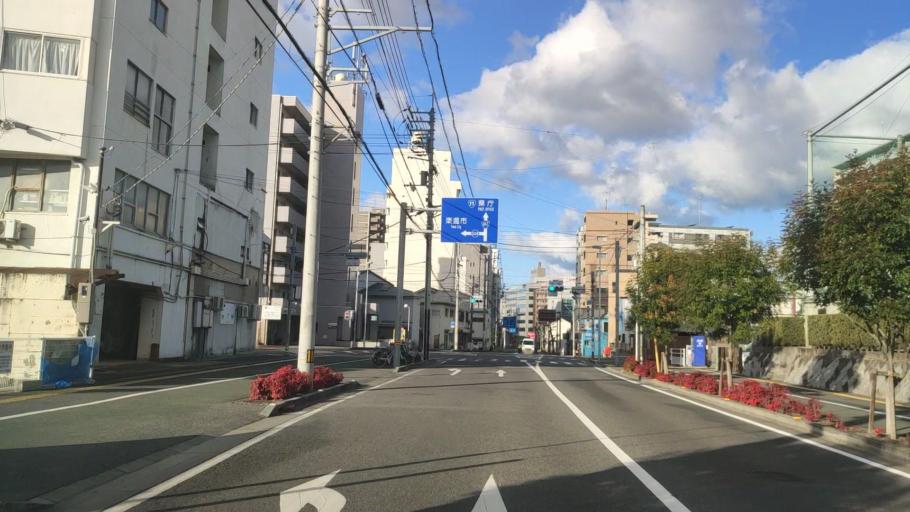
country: JP
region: Ehime
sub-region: Shikoku-chuo Shi
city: Matsuyama
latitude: 33.8414
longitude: 132.7788
